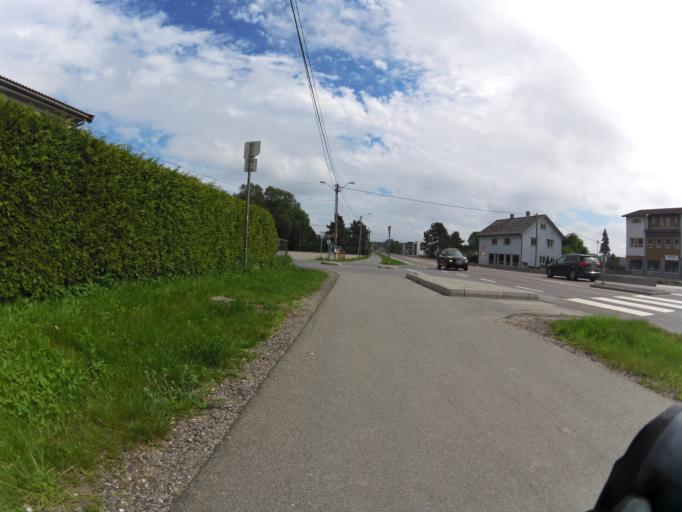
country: NO
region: Ostfold
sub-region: Rygge
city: Rygge
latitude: 59.3792
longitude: 10.7567
